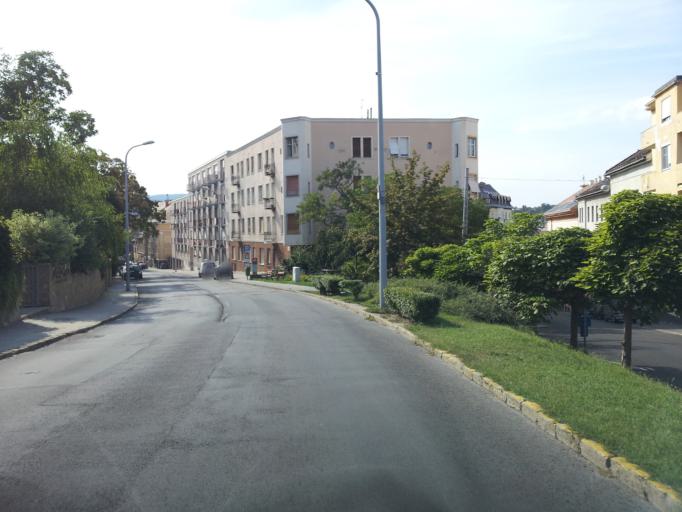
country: HU
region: Budapest
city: Budapest II. keruelet
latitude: 47.5059
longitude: 19.0294
